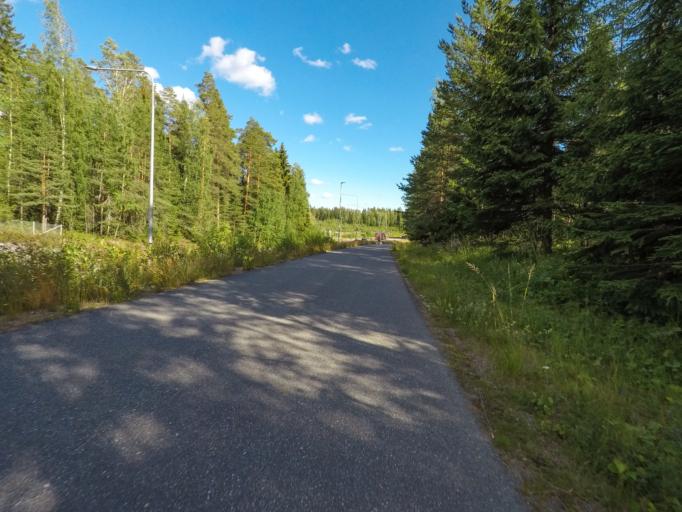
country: FI
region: South Karelia
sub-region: Lappeenranta
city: Lappeenranta
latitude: 61.0973
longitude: 28.1353
